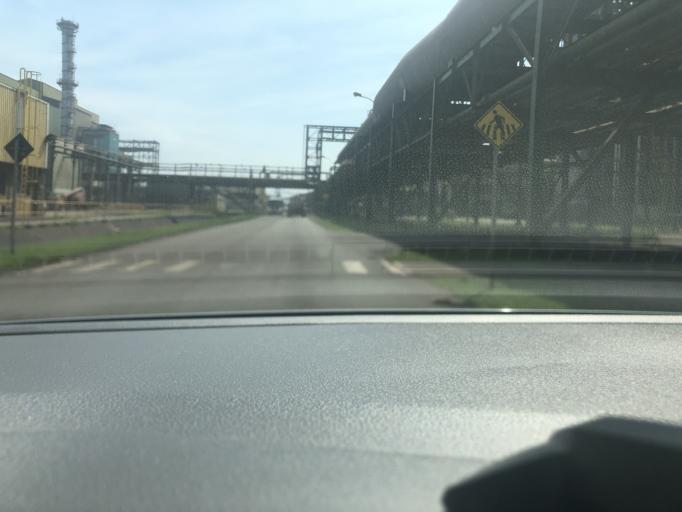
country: BR
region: Rio de Janeiro
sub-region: Itaguai
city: Itaguai
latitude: -22.9119
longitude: -43.7435
